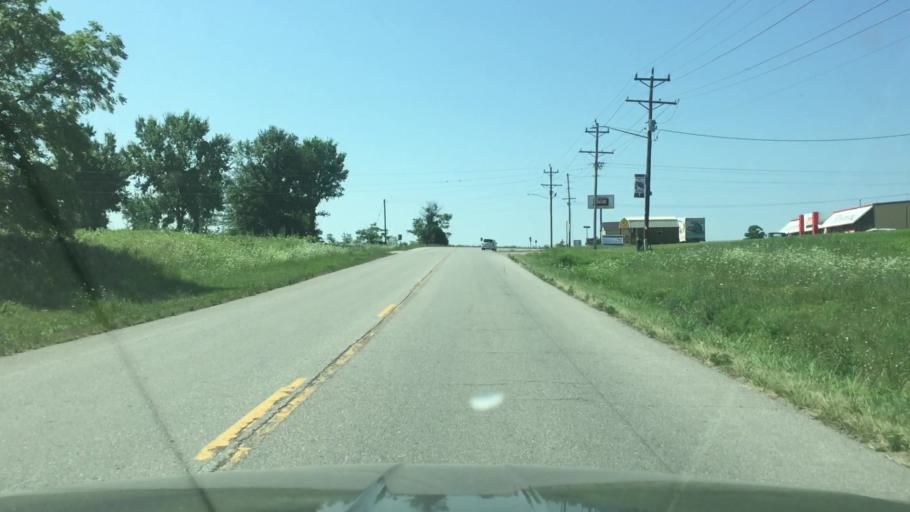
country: US
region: Missouri
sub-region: Moniteau County
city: Tipton
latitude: 38.6451
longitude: -92.7842
